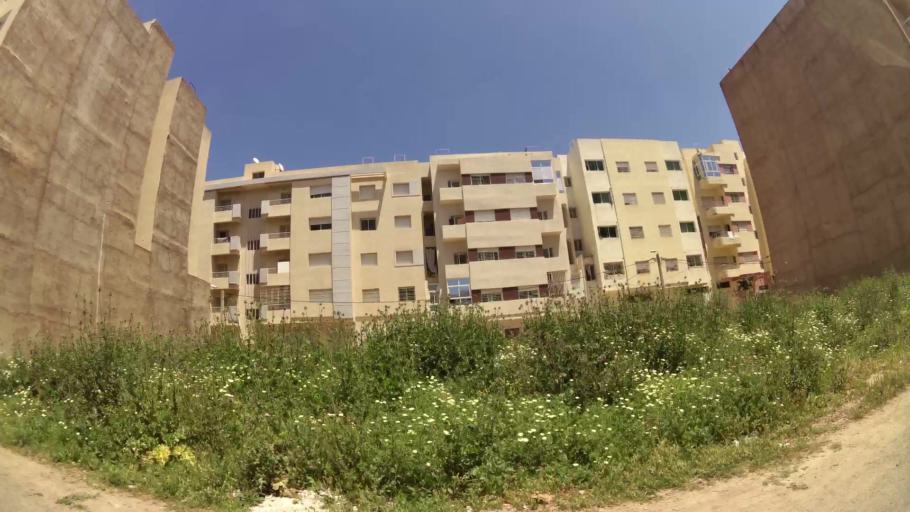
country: MA
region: Fes-Boulemane
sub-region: Fes
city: Fes
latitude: 34.0307
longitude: -5.0421
